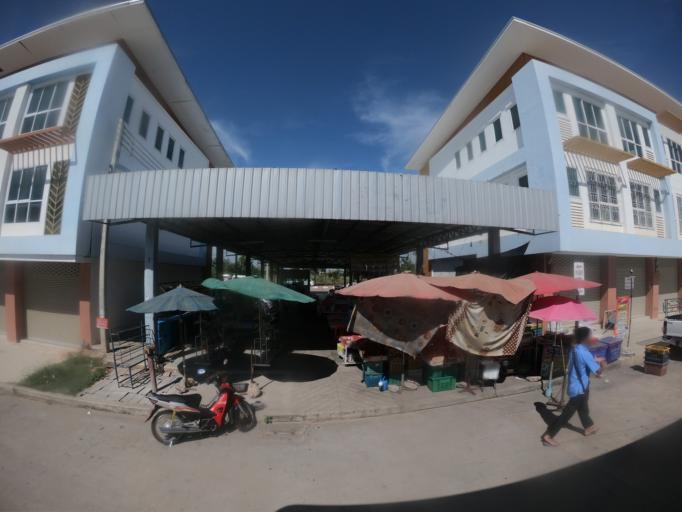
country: TH
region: Khon Kaen
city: Khon Kaen
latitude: 16.3895
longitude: 102.8038
